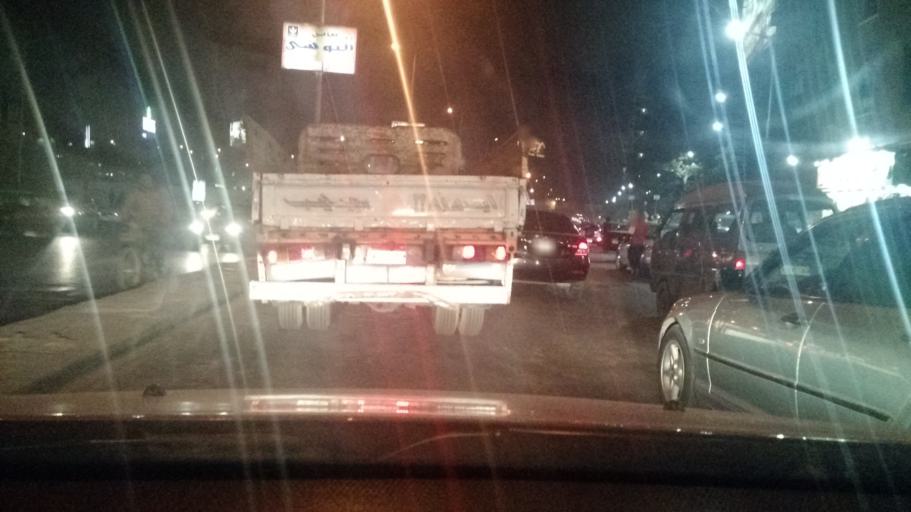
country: EG
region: Al Jizah
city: Al Jizah
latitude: 29.9895
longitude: 31.2153
